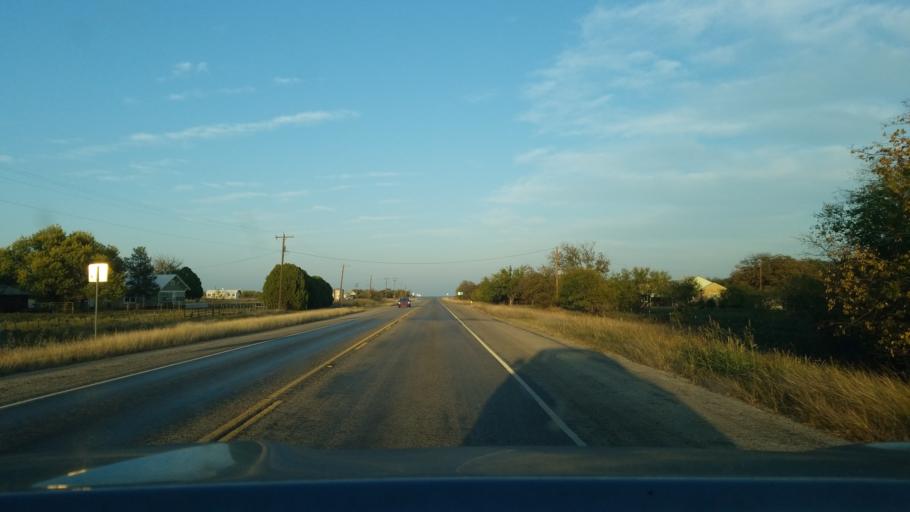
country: US
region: Texas
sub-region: Eastland County
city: Cisco
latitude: 32.3972
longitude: -98.9687
